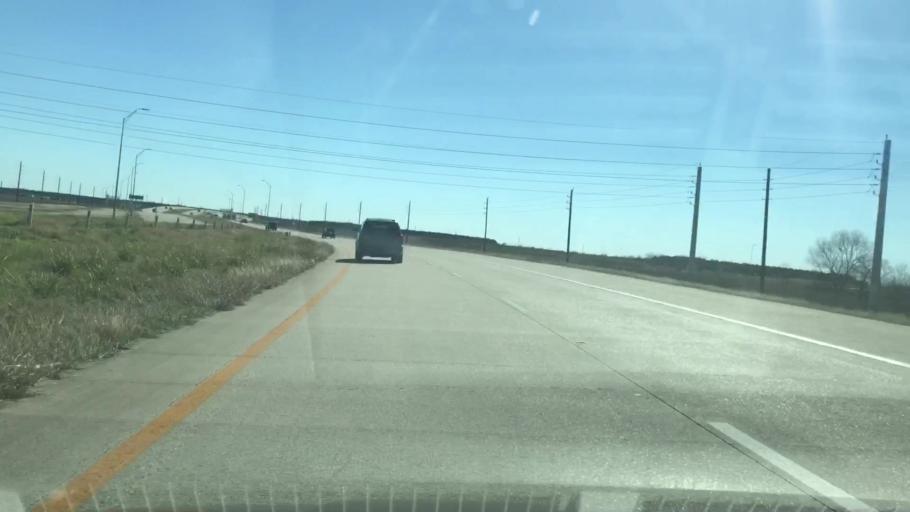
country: US
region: Texas
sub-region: Harris County
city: Cypress
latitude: 29.9127
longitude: -95.7621
